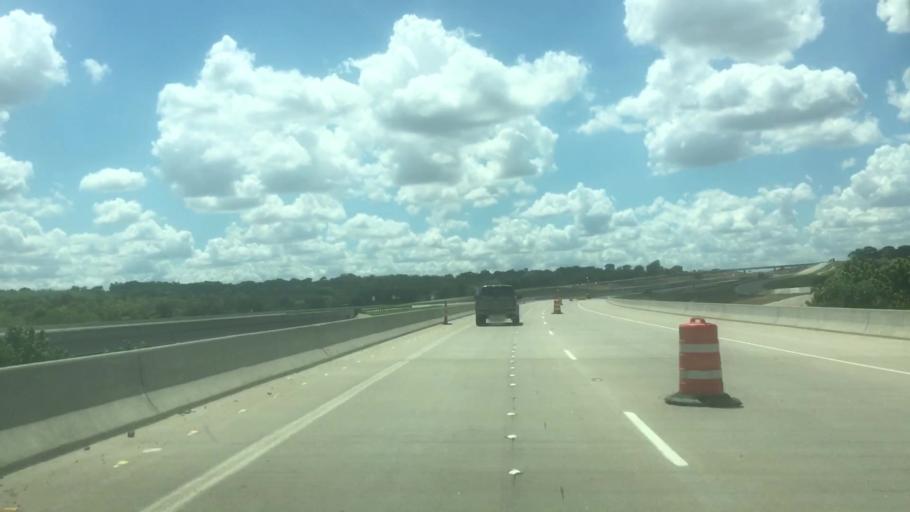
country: US
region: Texas
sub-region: Caldwell County
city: Lockhart
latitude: 29.8599
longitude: -97.7101
